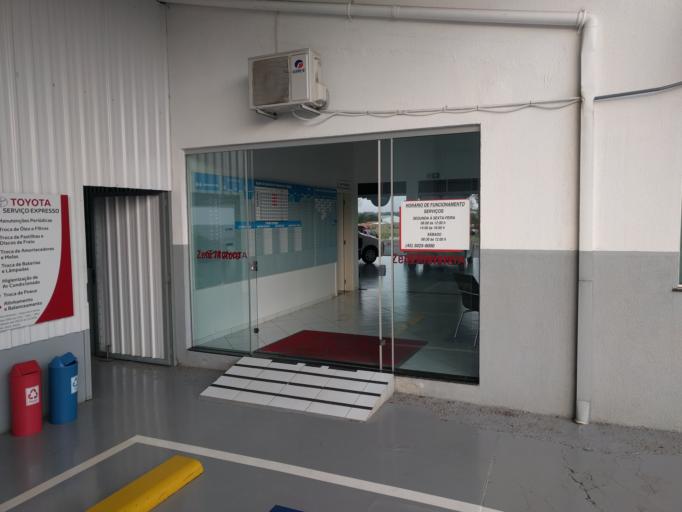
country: BR
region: Parana
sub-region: Foz Do Iguacu
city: Foz do Iguacu
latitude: -25.5228
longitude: -54.5632
